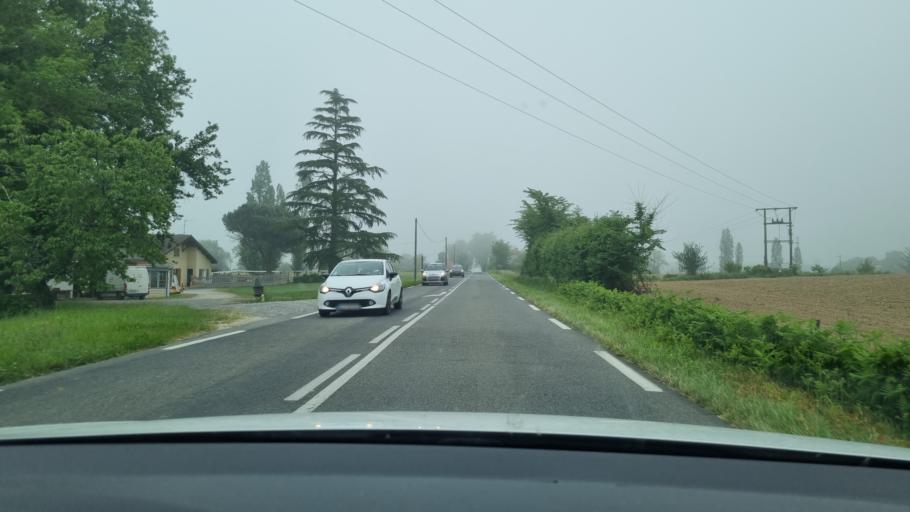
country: FR
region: Aquitaine
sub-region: Departement des Landes
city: Amou
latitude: 43.5358
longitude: -0.6905
